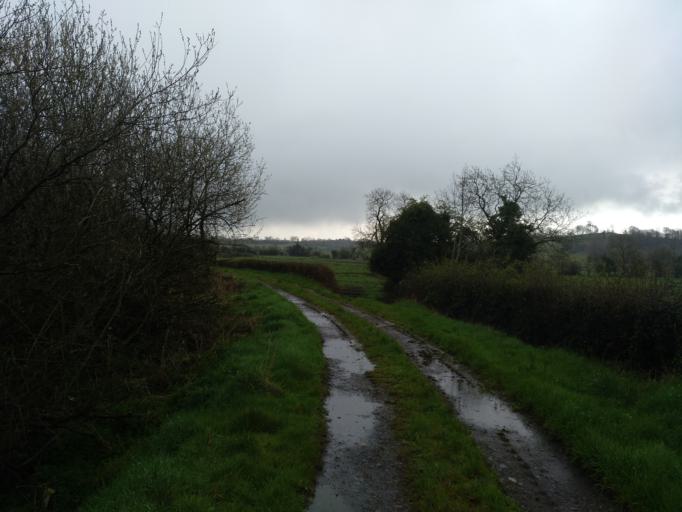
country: IE
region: Ulster
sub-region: County Monaghan
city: Clones
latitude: 54.1841
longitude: -7.1849
